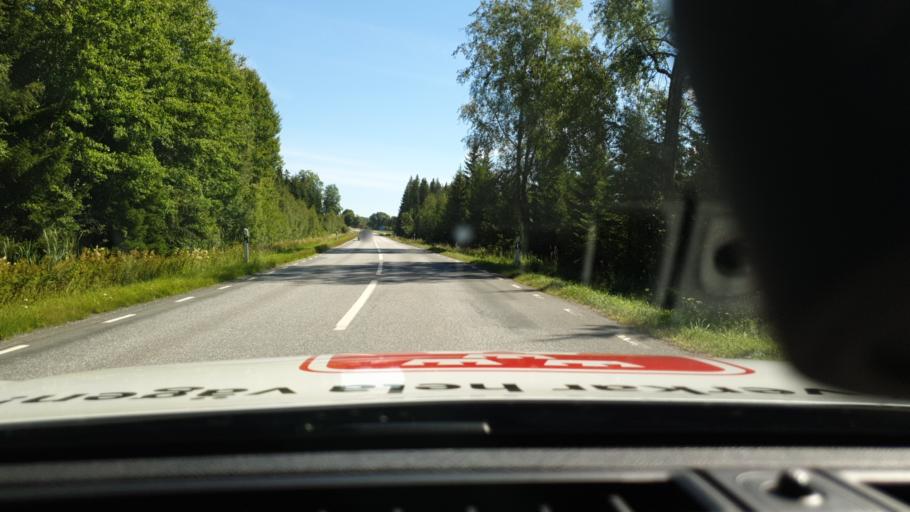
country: SE
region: Joenkoeping
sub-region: Aneby Kommun
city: Aneby
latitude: 57.9750
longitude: 14.7753
